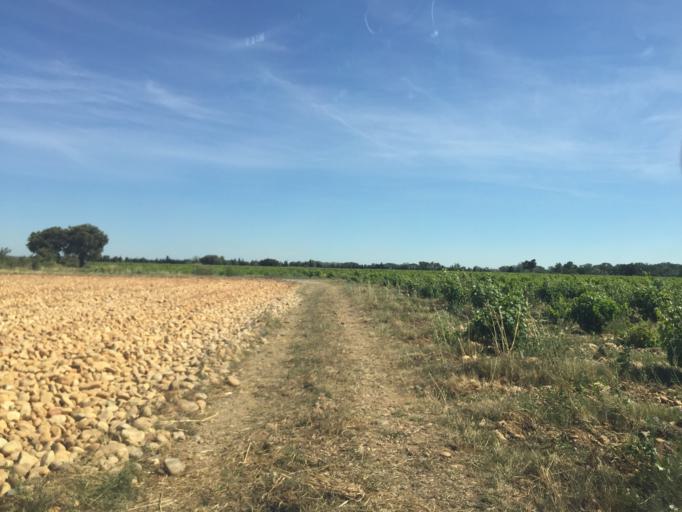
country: FR
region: Provence-Alpes-Cote d'Azur
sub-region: Departement du Vaucluse
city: Chateauneuf-du-Pape
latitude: 44.0380
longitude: 4.8396
